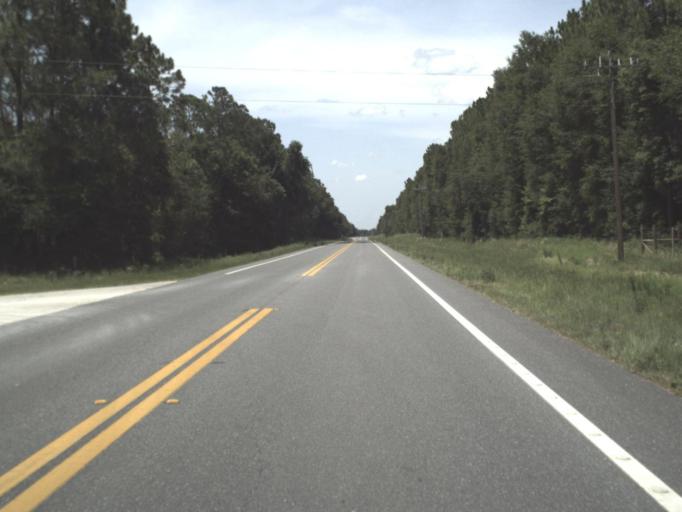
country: US
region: Florida
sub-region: Gilchrist County
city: Trenton
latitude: 29.8451
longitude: -82.8650
